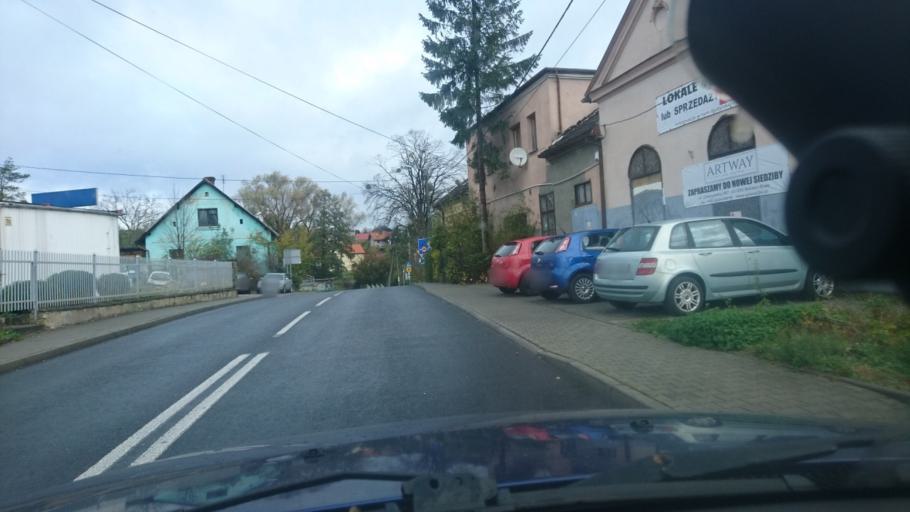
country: PL
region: Silesian Voivodeship
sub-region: Bielsko-Biala
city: Bielsko-Biala
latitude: 49.8245
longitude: 19.0123
